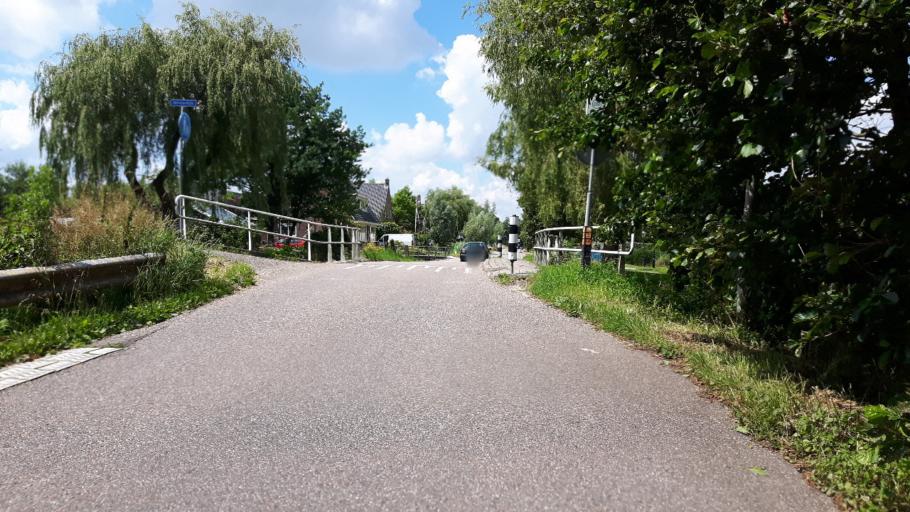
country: NL
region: South Holland
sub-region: Gemeente Waddinxveen
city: Oranjewijk
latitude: 52.0441
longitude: 4.6743
